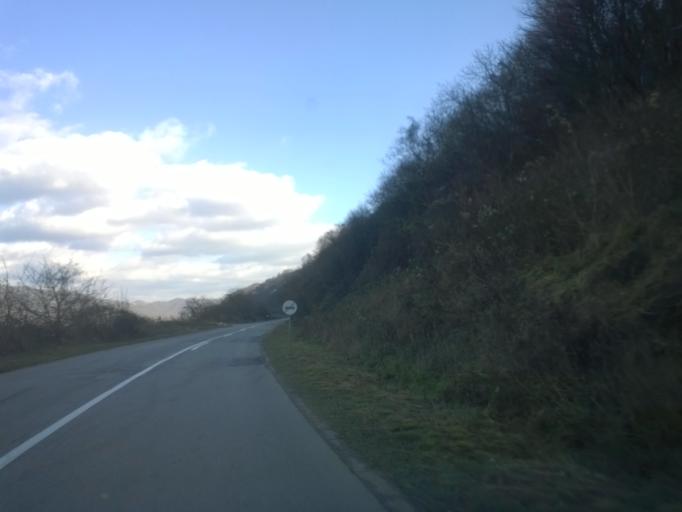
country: RO
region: Caras-Severin
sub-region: Comuna Pescari
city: Coronini
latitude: 44.6536
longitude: 21.7454
